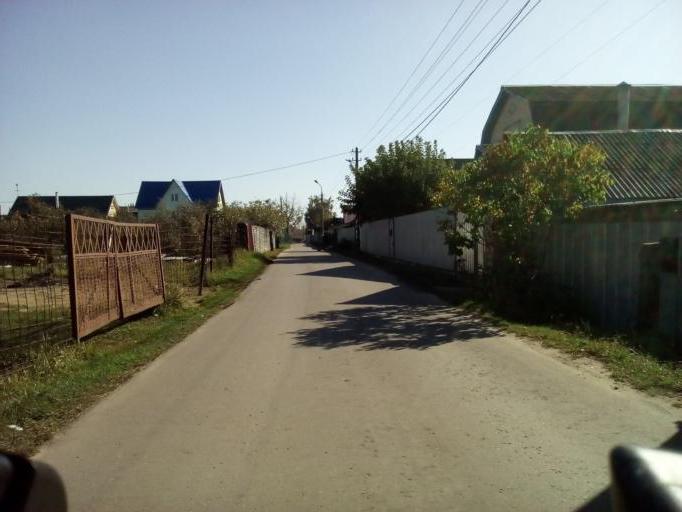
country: RU
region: Moskovskaya
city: Ramenskoye
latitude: 55.5493
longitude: 38.2850
